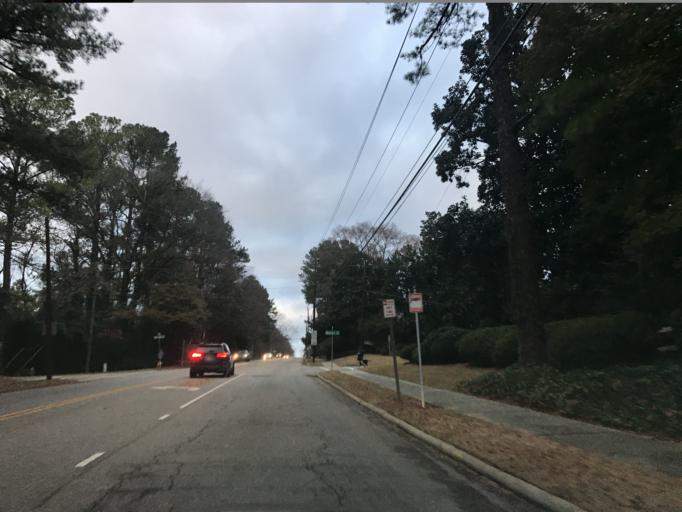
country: US
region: North Carolina
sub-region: Wake County
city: West Raleigh
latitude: 35.8285
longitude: -78.6487
